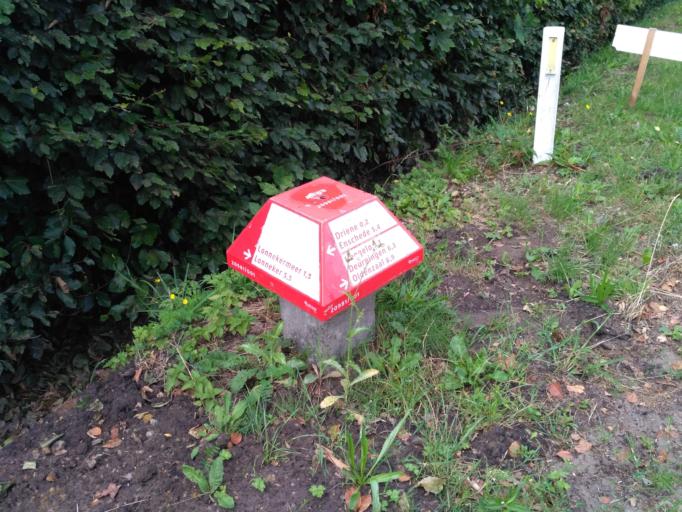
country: NL
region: Overijssel
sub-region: Gemeente Hengelo
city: Hengelo
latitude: 52.2665
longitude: 6.8427
